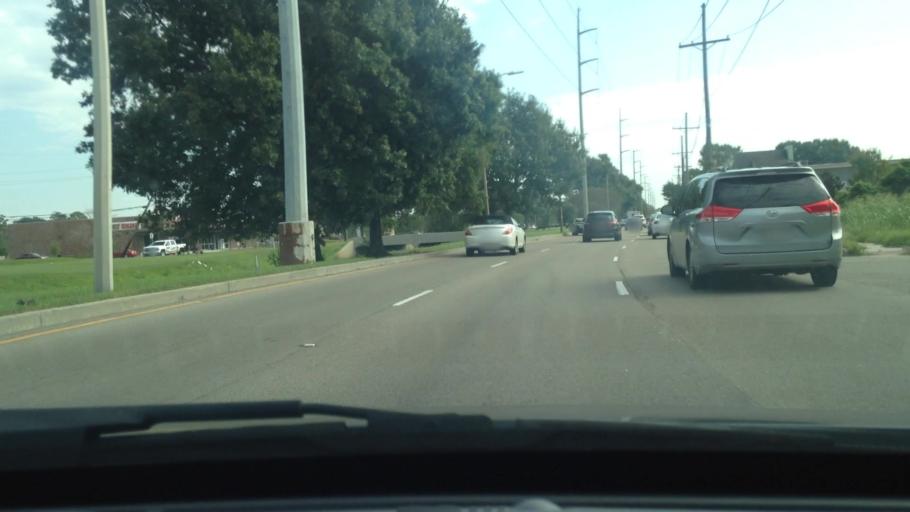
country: US
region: Louisiana
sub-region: Jefferson Parish
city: Terrytown
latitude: 29.9285
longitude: -90.0303
